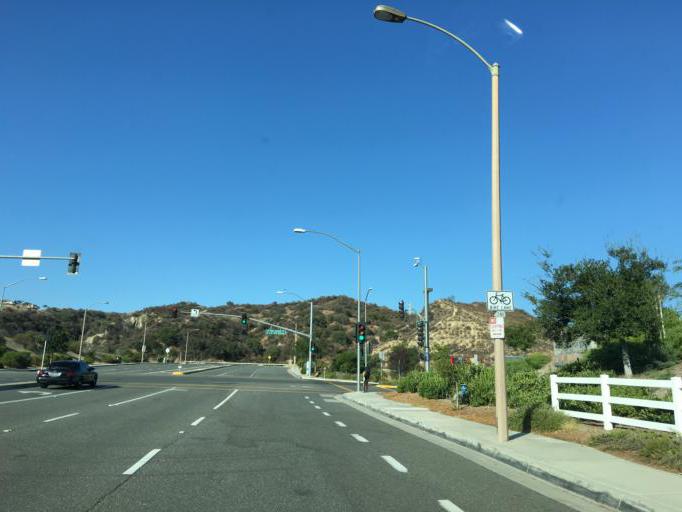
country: US
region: California
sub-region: Los Angeles County
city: Valencia
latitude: 34.4019
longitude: -118.5952
